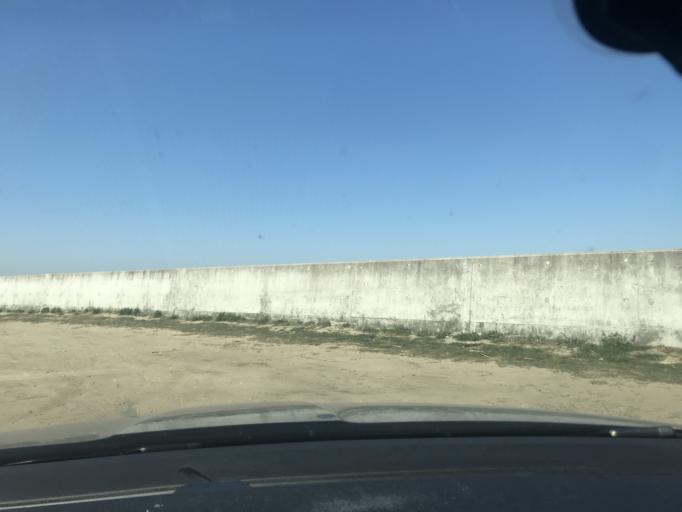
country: PL
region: Pomeranian Voivodeship
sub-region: Powiat pucki
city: Mosty
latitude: 54.6308
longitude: 18.4922
